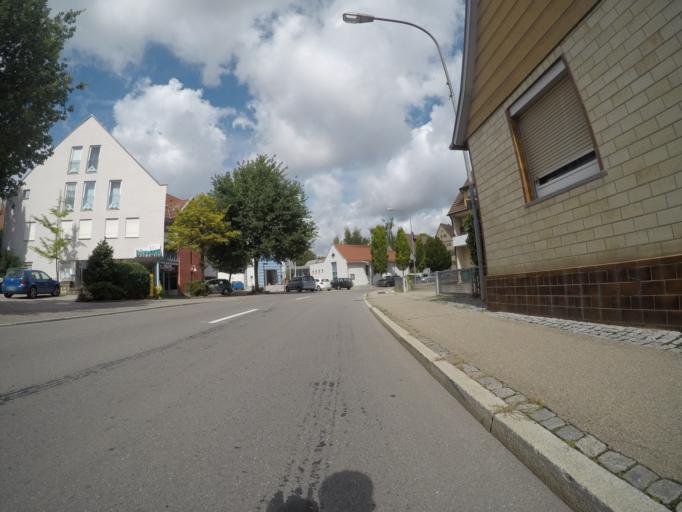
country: DE
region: Baden-Wuerttemberg
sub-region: Regierungsbezirk Stuttgart
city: Aidlingen
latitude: 48.6784
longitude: 8.8946
